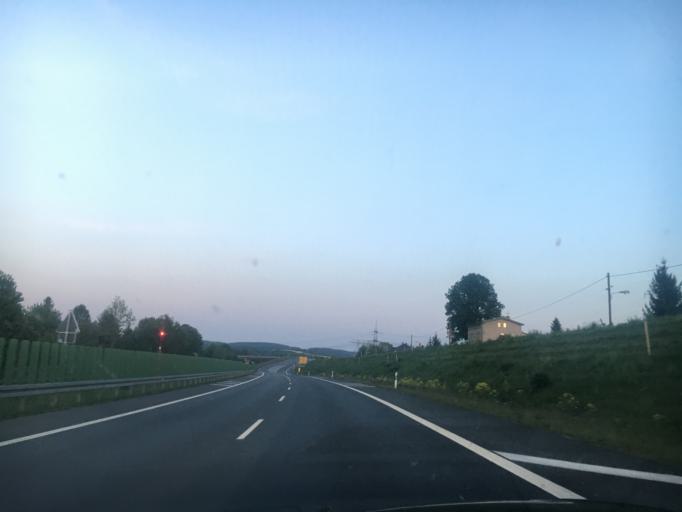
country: DE
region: Thuringia
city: Crimla
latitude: 50.8293
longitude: 12.0728
